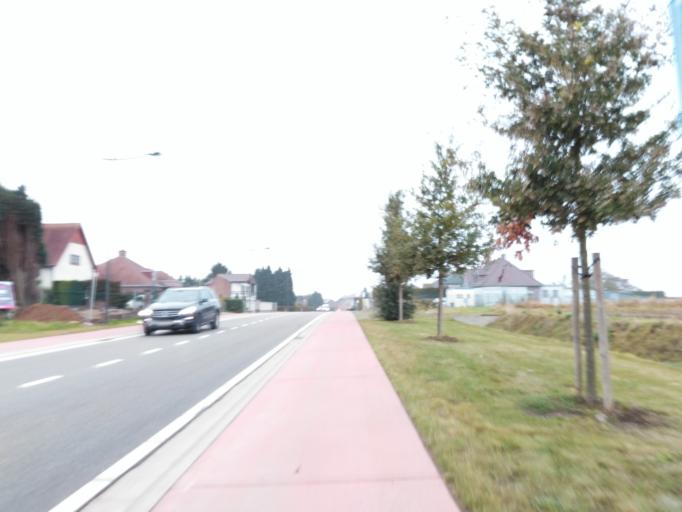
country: BE
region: Flanders
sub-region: Provincie Limburg
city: Riemst
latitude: 50.8615
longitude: 5.5893
